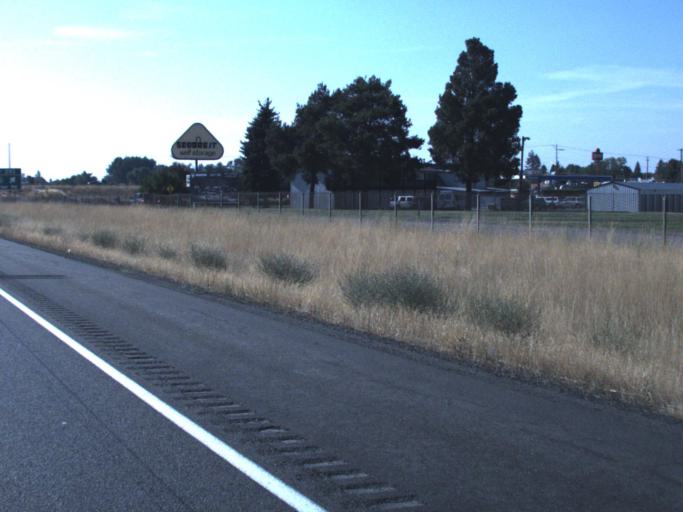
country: US
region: Washington
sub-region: Spokane County
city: Liberty Lake
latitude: 47.6657
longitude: -117.1498
